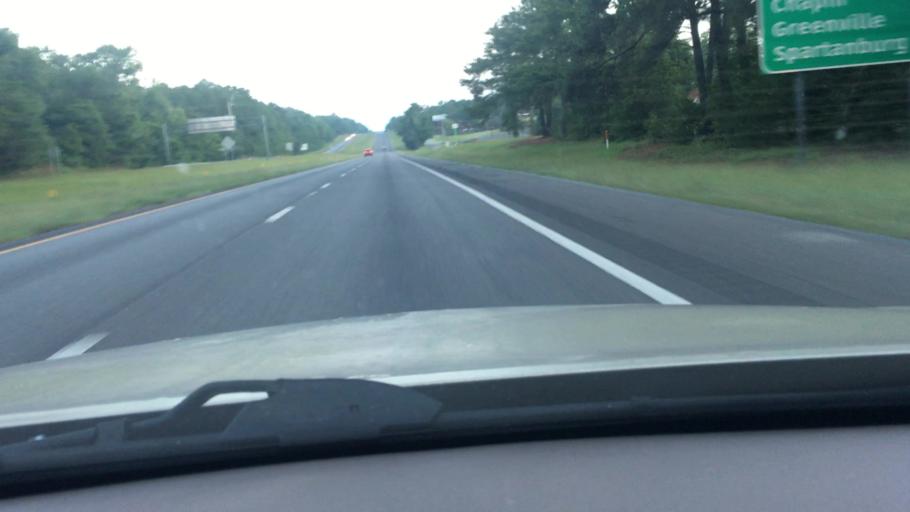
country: US
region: South Carolina
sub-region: Lexington County
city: Irmo
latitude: 34.1090
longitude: -81.1850
